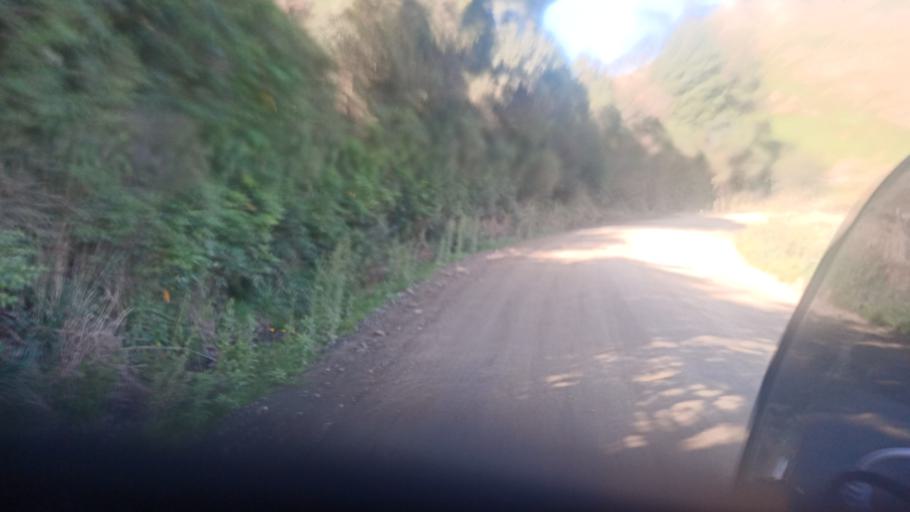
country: NZ
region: Gisborne
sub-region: Gisborne District
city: Gisborne
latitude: -38.4332
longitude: 177.5551
